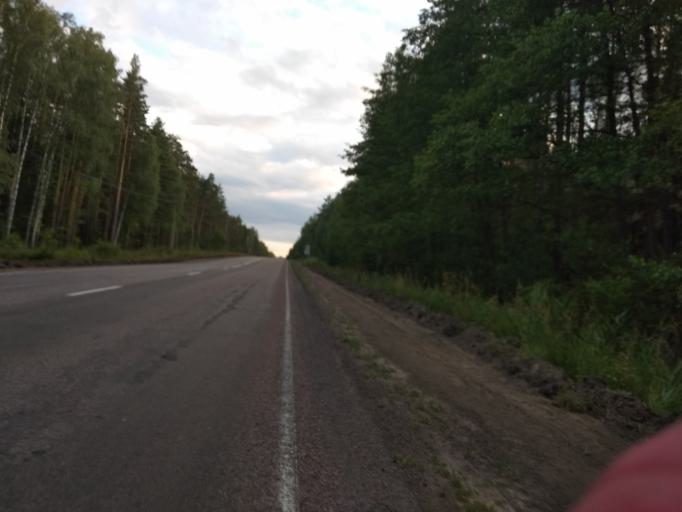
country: RU
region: Moskovskaya
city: Misheronskiy
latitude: 55.6402
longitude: 39.7528
